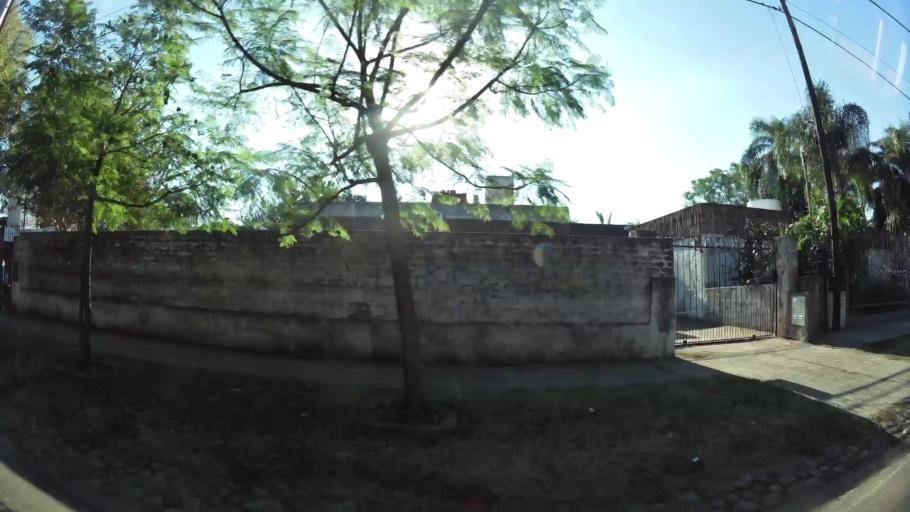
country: AR
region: Cordoba
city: Villa Allende
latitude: -31.3580
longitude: -64.2469
